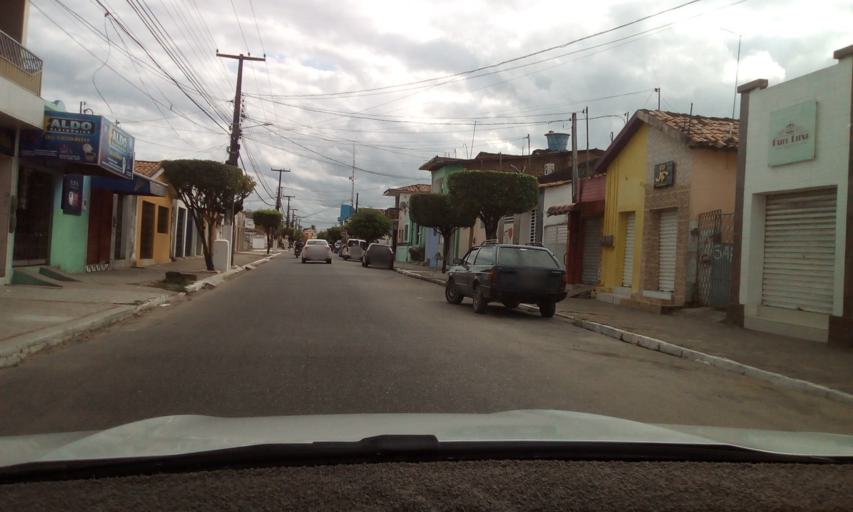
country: BR
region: Paraiba
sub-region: Mamanguape
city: Mamanguape
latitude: -6.8369
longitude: -35.1288
